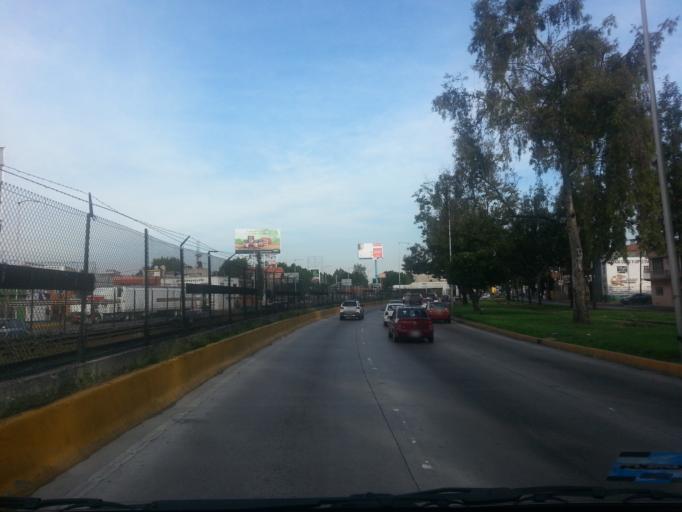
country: MX
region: Mexico City
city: Venustiano Carranza
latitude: 19.4537
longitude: -99.1113
